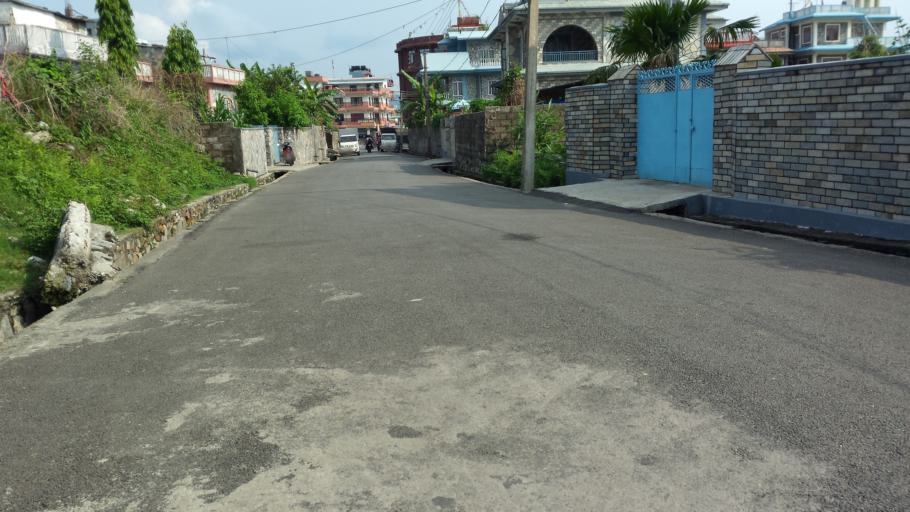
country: NP
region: Western Region
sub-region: Gandaki Zone
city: Pokhara
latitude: 28.2080
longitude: 83.9991
